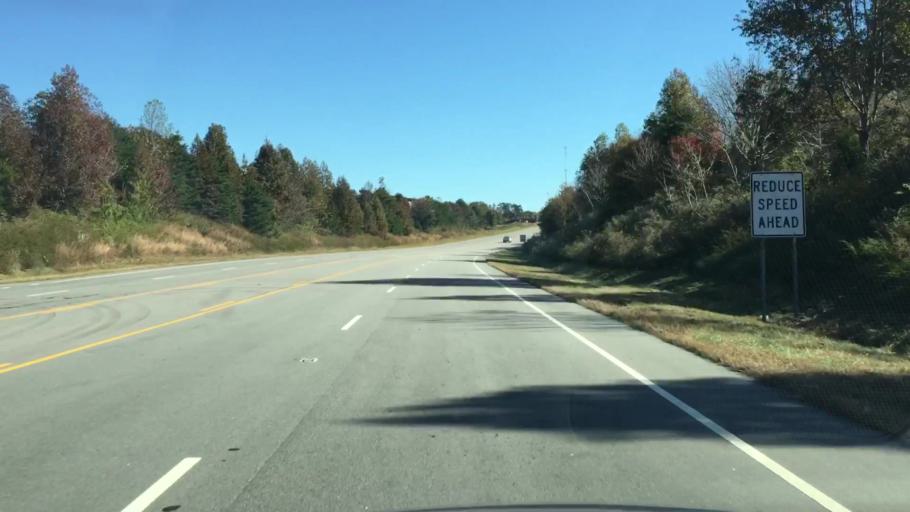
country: US
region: North Carolina
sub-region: Rockingham County
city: Reidsville
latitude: 36.3123
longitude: -79.6391
